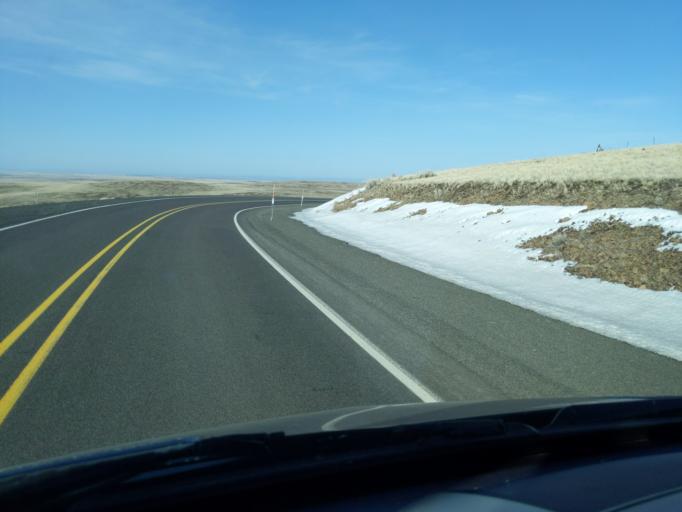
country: US
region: Oregon
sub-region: Umatilla County
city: Pilot Rock
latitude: 45.3005
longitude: -119.0064
